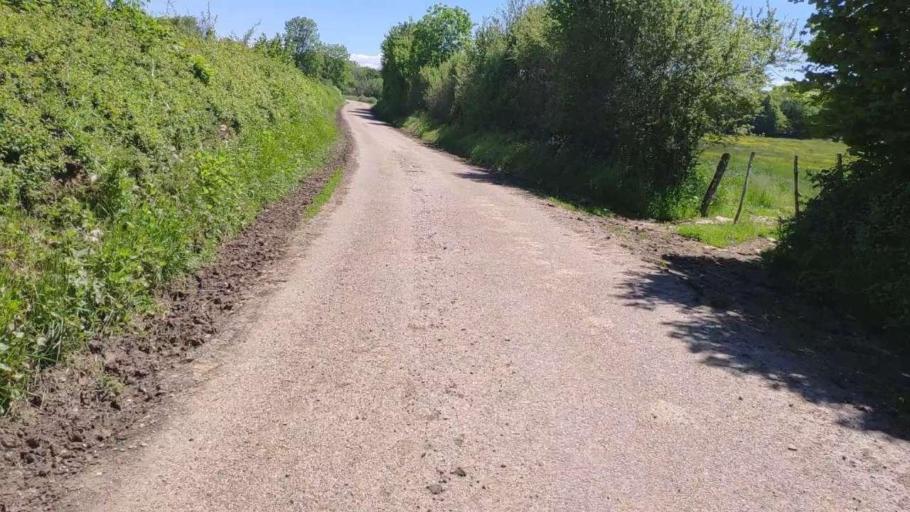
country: FR
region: Franche-Comte
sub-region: Departement du Jura
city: Perrigny
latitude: 46.7123
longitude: 5.6531
